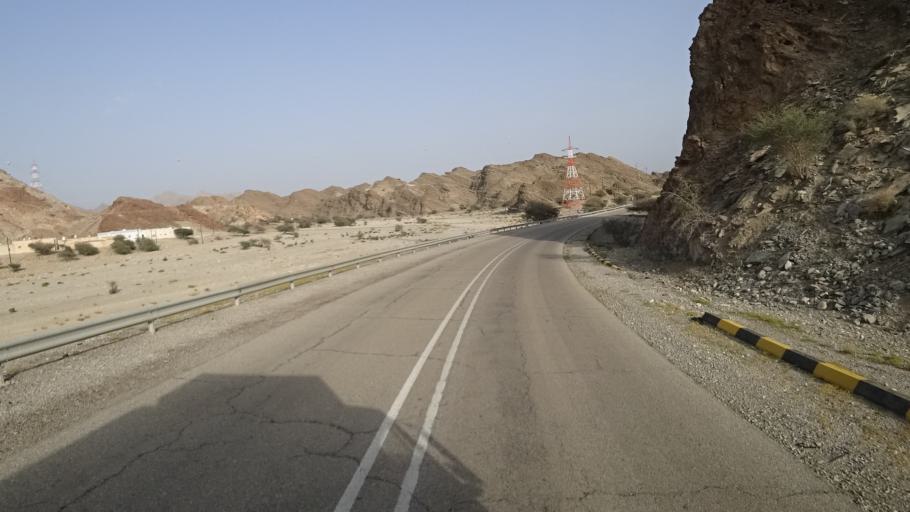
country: OM
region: Muhafazat Masqat
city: Bawshar
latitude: 23.3573
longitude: 58.5326
